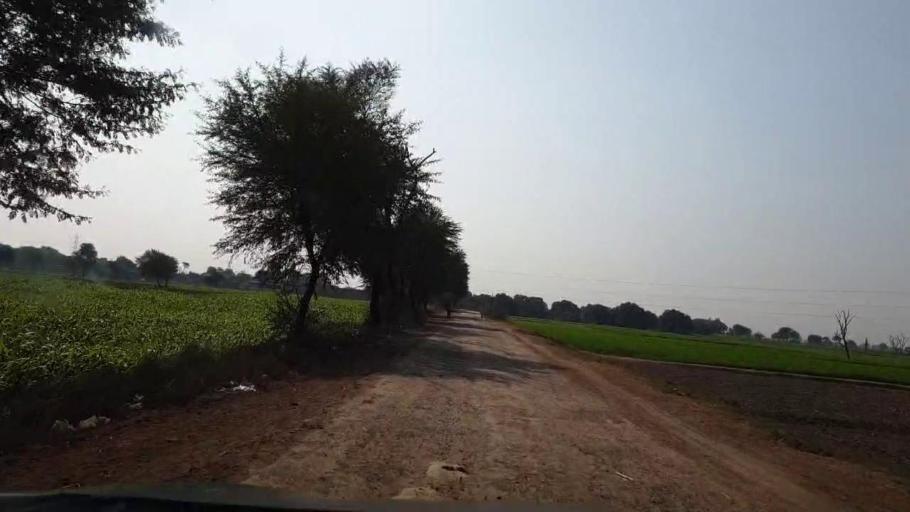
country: PK
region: Sindh
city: Bhit Shah
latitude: 25.7503
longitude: 68.5053
